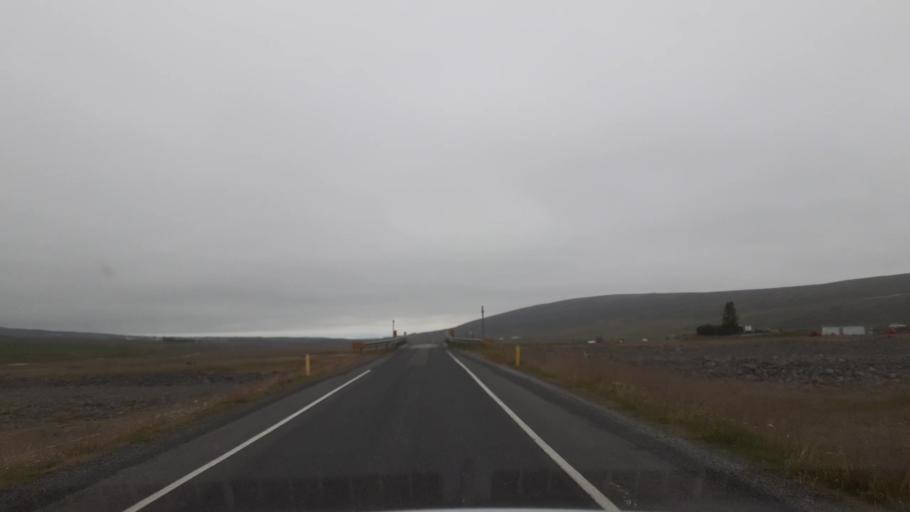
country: IS
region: Northeast
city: Siglufjoerdur
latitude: 65.7393
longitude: -19.1368
